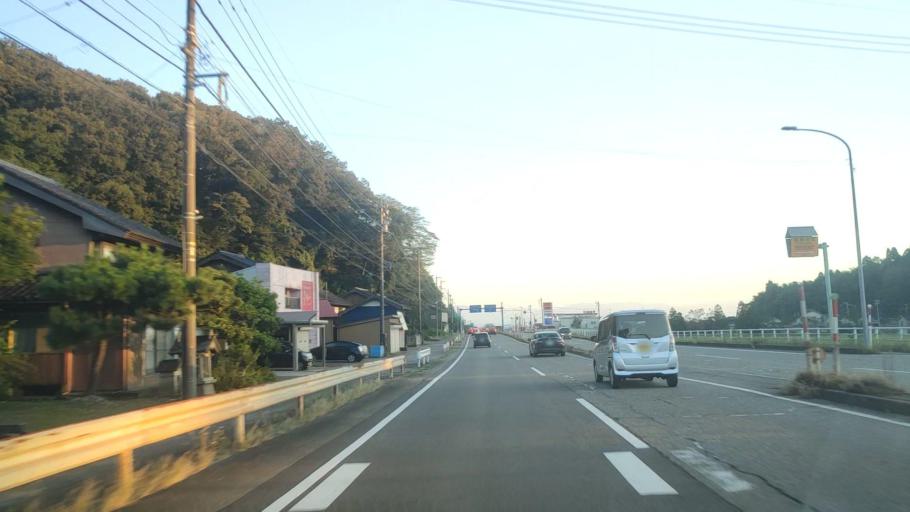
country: JP
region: Toyama
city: Takaoka
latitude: 36.7838
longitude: 136.9999
